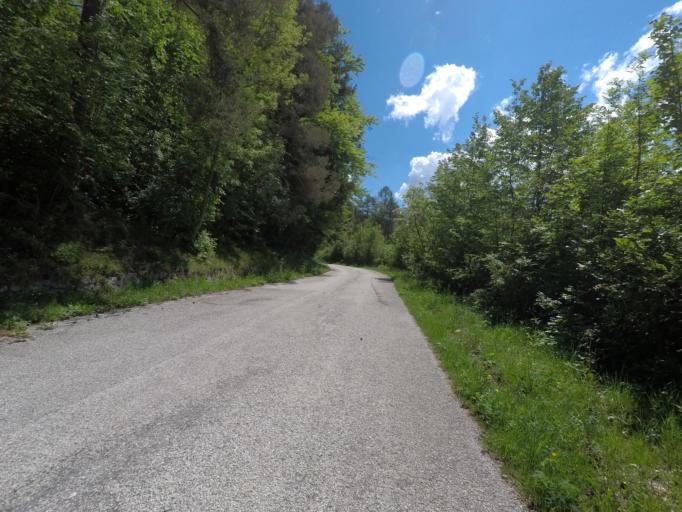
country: IT
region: Friuli Venezia Giulia
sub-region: Provincia di Udine
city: Raveo
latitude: 46.4440
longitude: 12.8799
